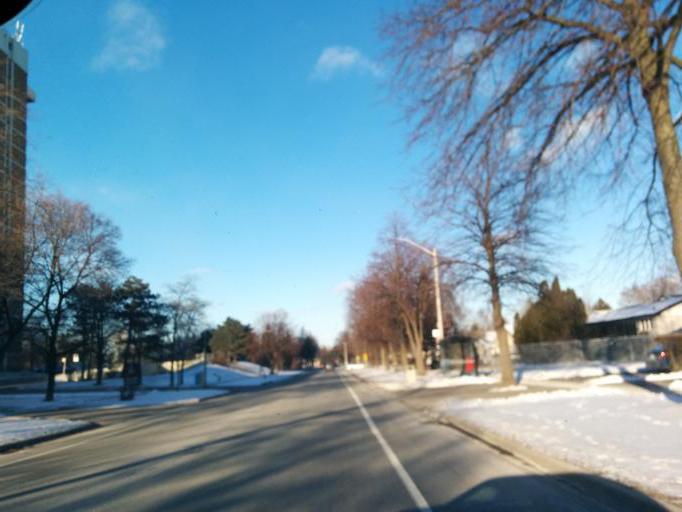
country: CA
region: Ontario
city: Mississauga
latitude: 43.5134
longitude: -79.6460
